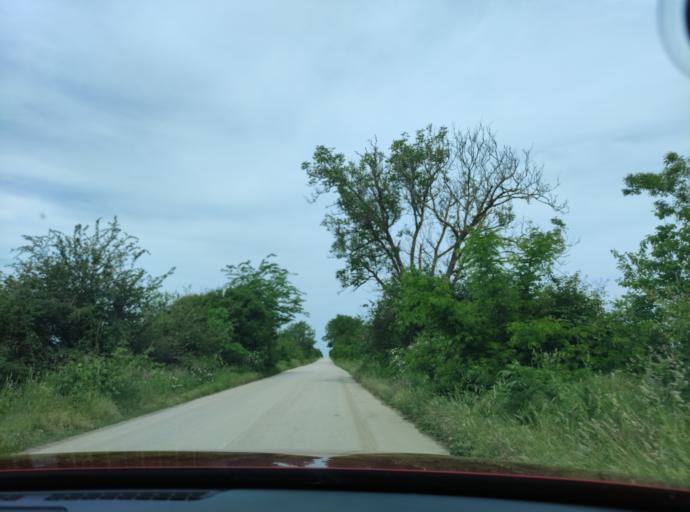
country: BG
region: Pleven
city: Iskur
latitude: 43.5241
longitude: 24.3199
